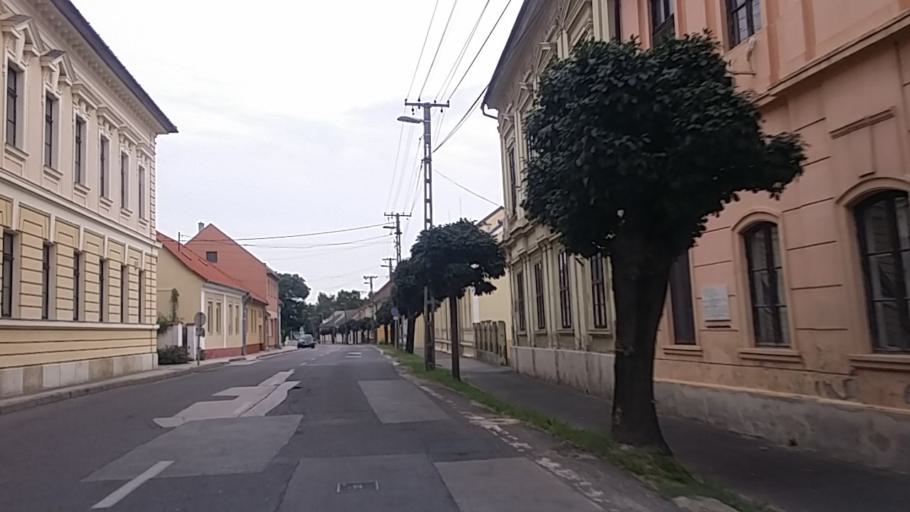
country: HU
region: Tolna
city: Paks
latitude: 46.6285
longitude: 18.8688
